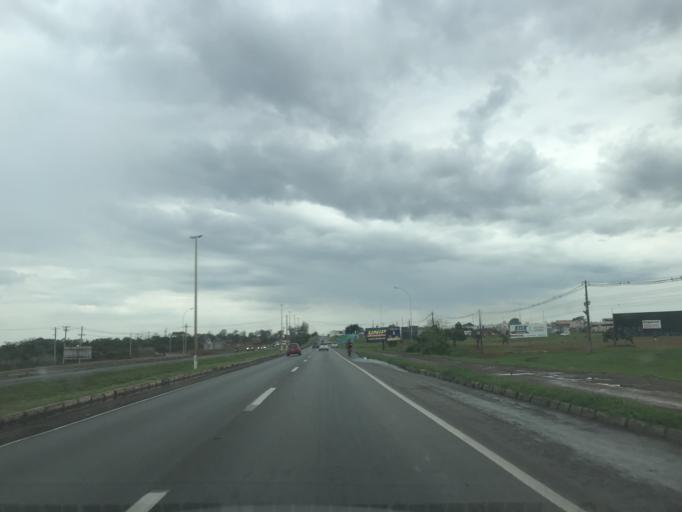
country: BR
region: Federal District
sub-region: Brasilia
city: Brasilia
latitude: -16.0067
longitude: -47.9834
